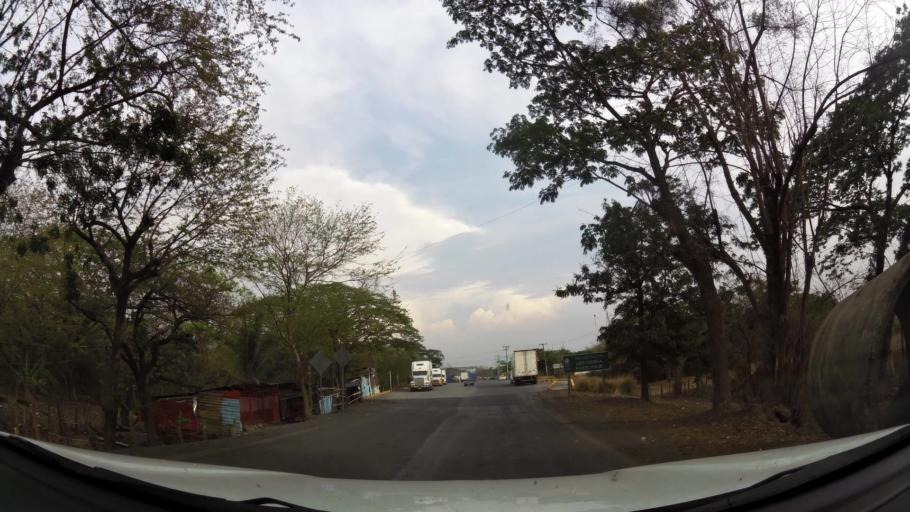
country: NI
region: Rivas
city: Cardenas
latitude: 11.2203
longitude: -85.6150
